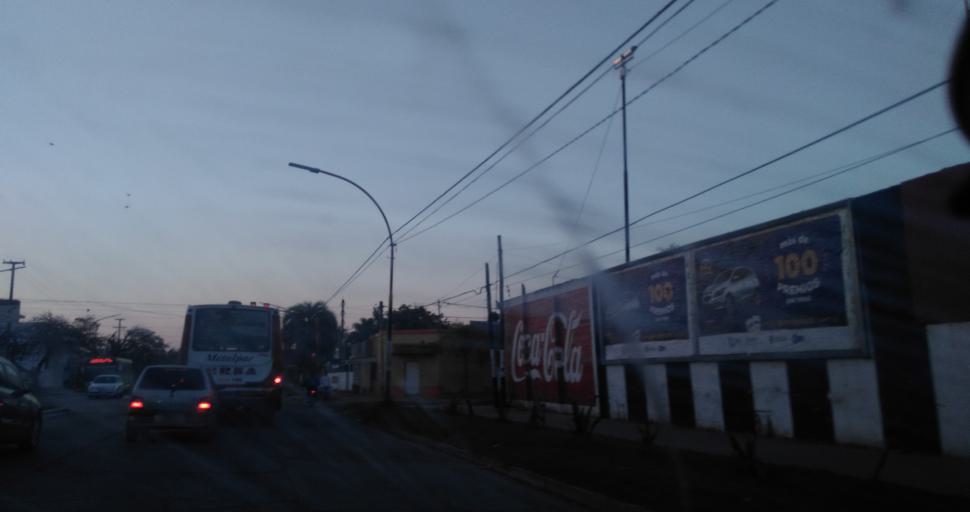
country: AR
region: Chaco
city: Resistencia
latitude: -27.4693
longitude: -58.9662
